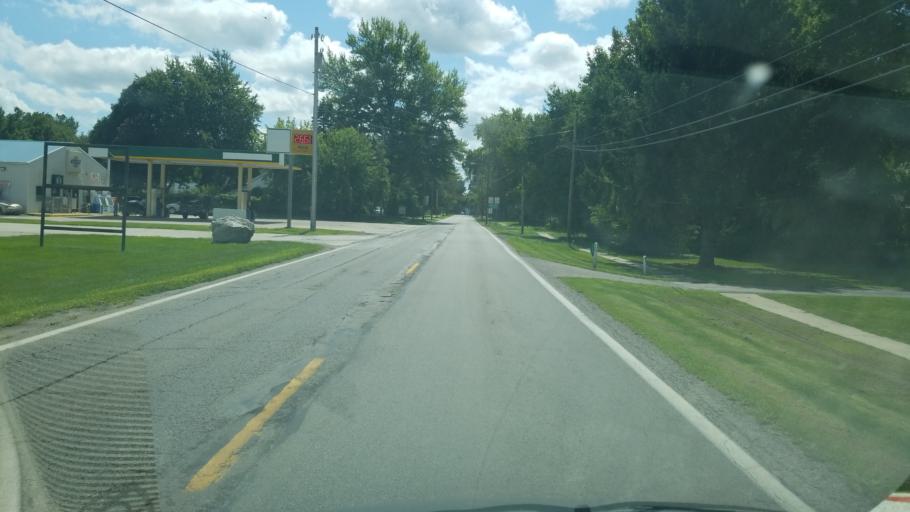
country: US
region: Ohio
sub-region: Henry County
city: Liberty Center
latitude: 41.4511
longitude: -84.0088
